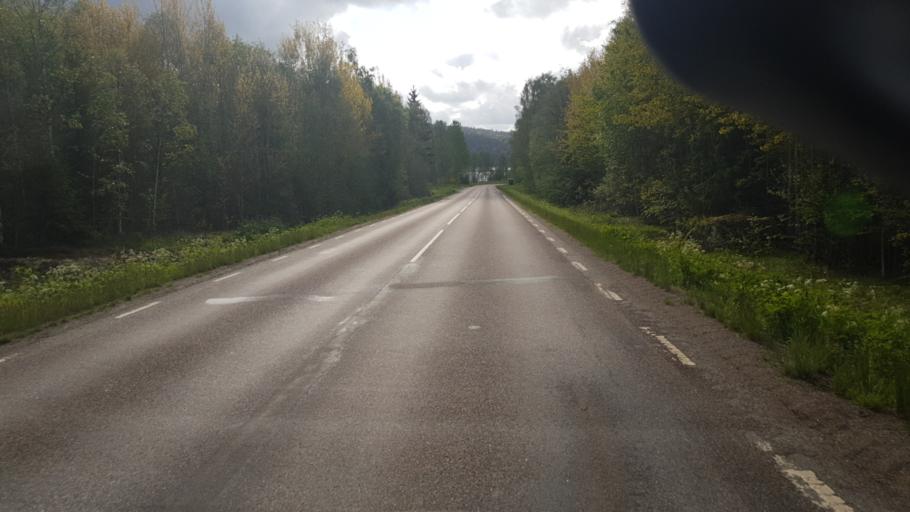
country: SE
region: Vaermland
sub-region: Eda Kommun
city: Amotfors
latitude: 59.6979
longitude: 12.3317
